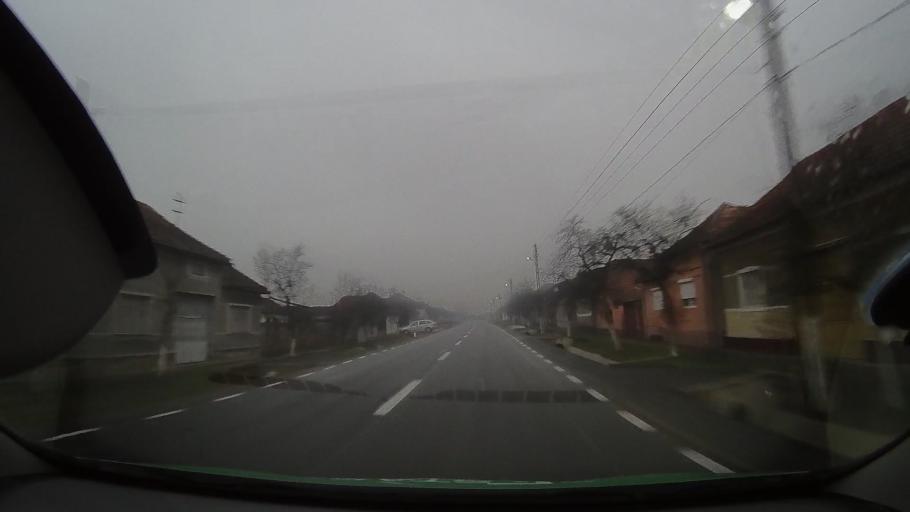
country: RO
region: Bihor
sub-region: Comuna Olcea
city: Calacea
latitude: 46.6346
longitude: 21.9569
